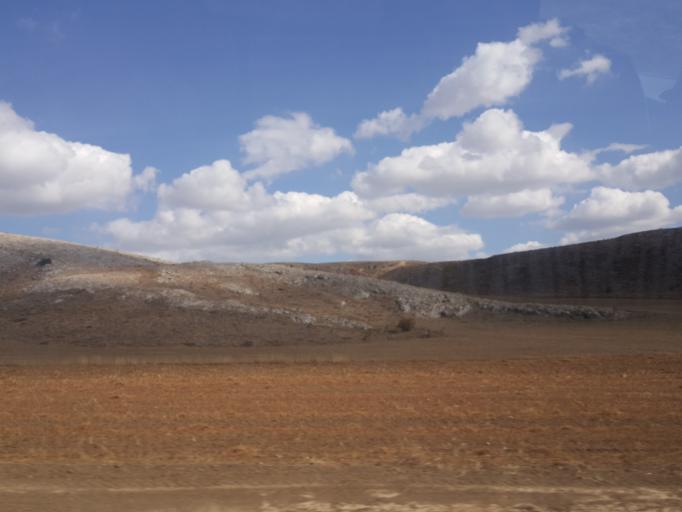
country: TR
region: Tokat
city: Artova
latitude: 40.1338
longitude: 36.3503
